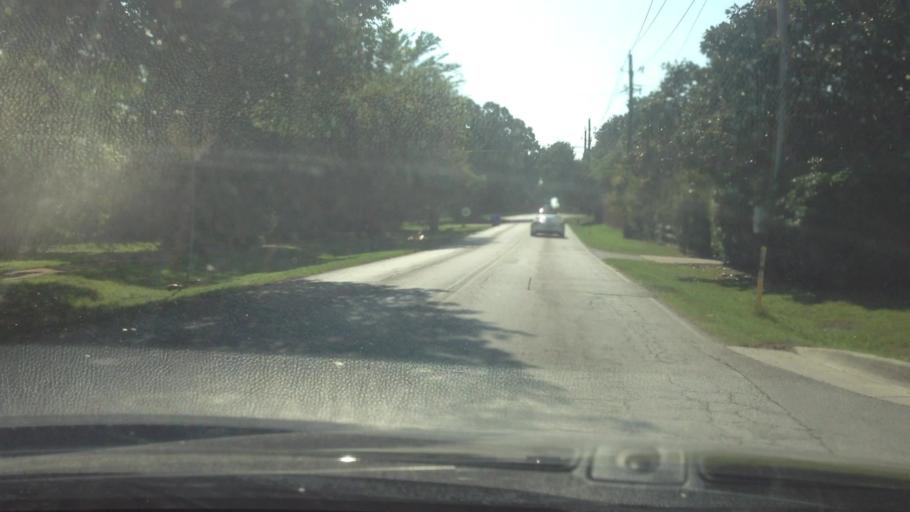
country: US
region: Texas
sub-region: Tarrant County
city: Colleyville
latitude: 32.9003
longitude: -97.1438
